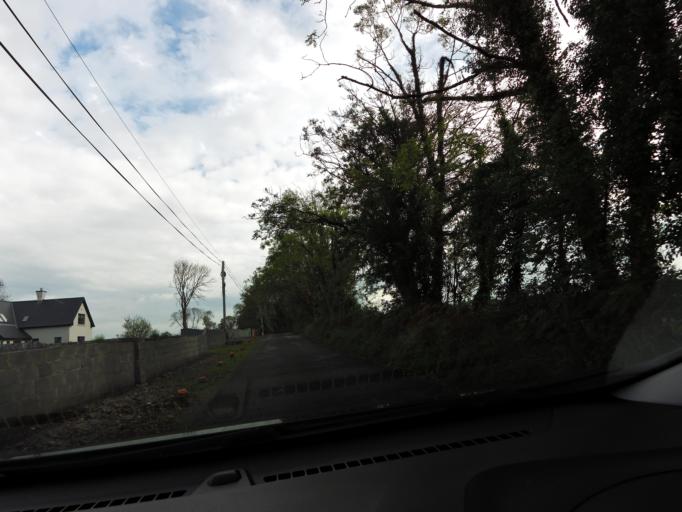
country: IE
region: Connaught
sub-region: County Galway
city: Athenry
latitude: 53.2388
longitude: -8.7411
